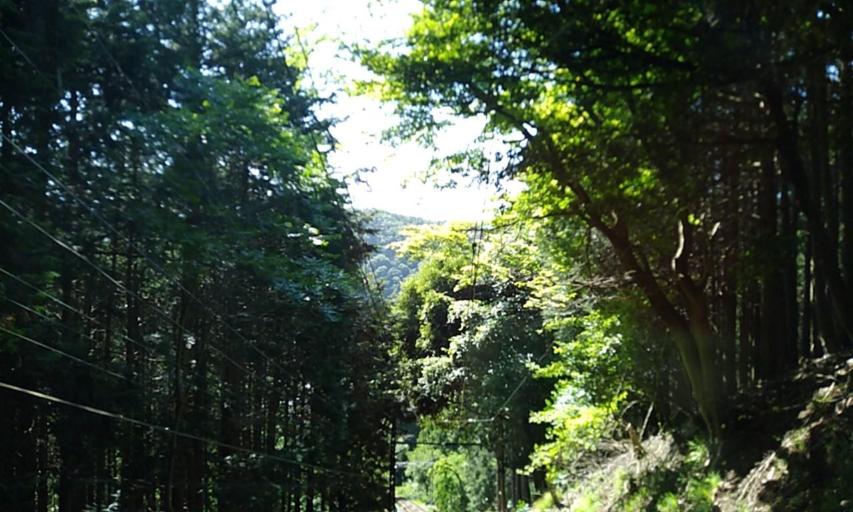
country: JP
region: Kyoto
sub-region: Kyoto-shi
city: Kamigyo-ku
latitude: 35.0668
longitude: 135.8139
